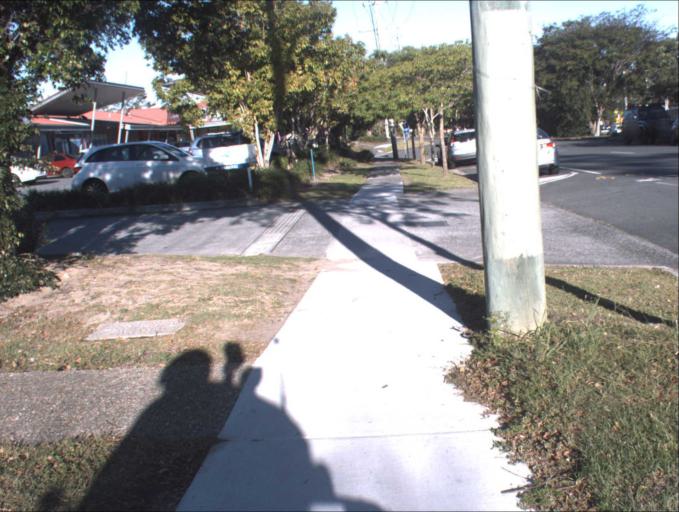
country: AU
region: Queensland
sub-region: Logan
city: Logan City
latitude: -27.6420
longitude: 153.1173
